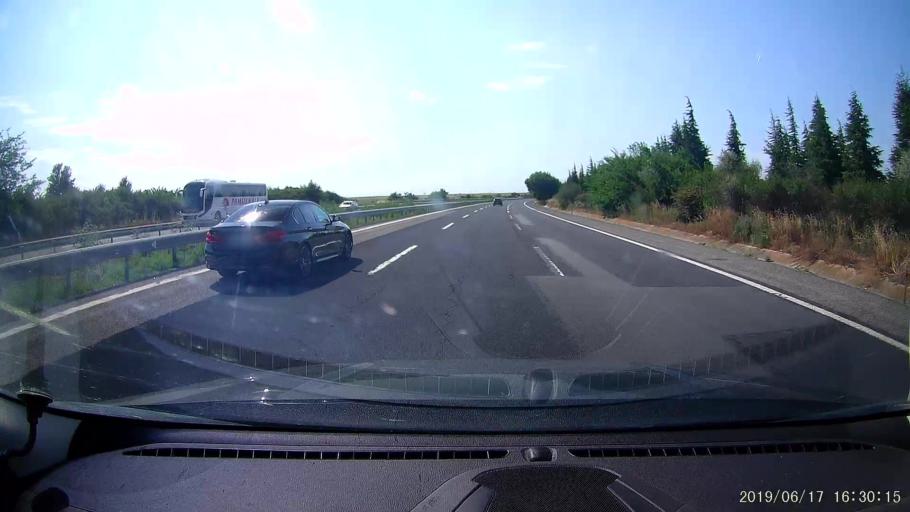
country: TR
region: Tekirdag
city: Beyazkoy
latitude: 41.3437
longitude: 27.6587
